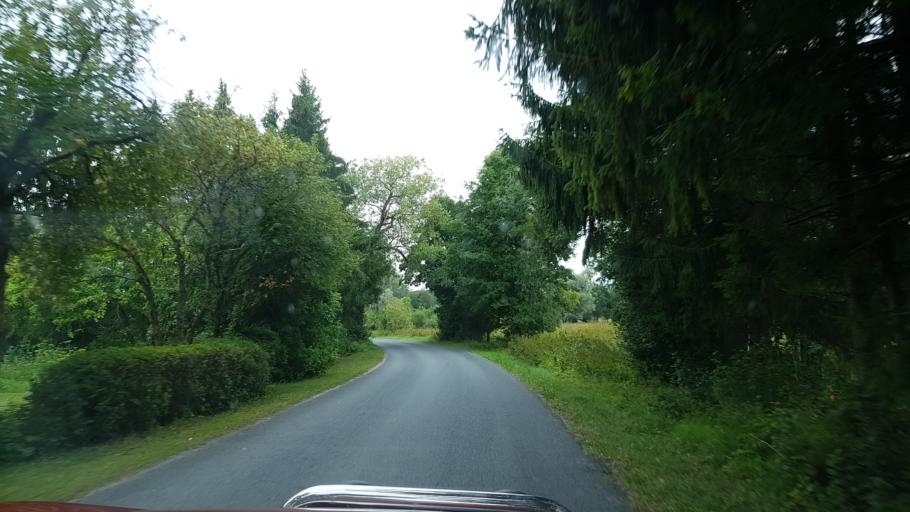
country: EE
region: Laeaene
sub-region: Ridala Parish
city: Uuemoisa
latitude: 58.8019
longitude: 23.6636
